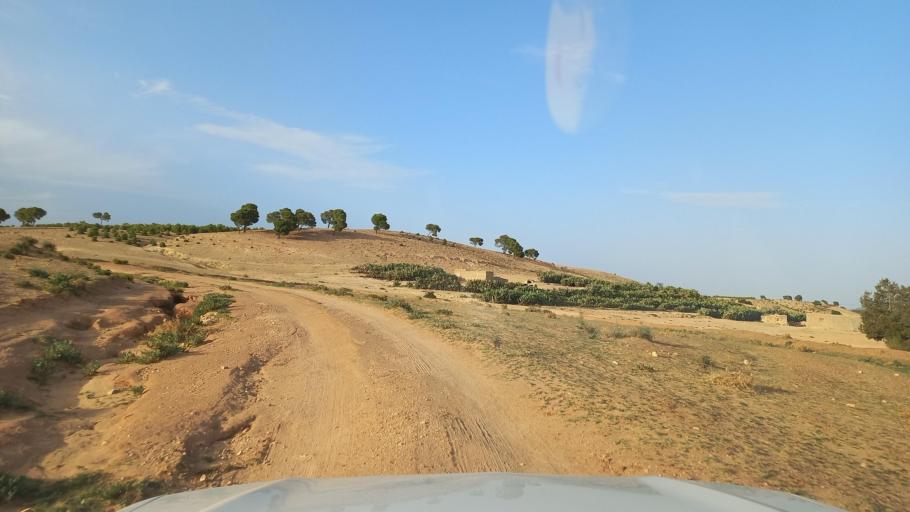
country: TN
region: Al Qasrayn
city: Sbiba
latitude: 35.4089
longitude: 8.8987
